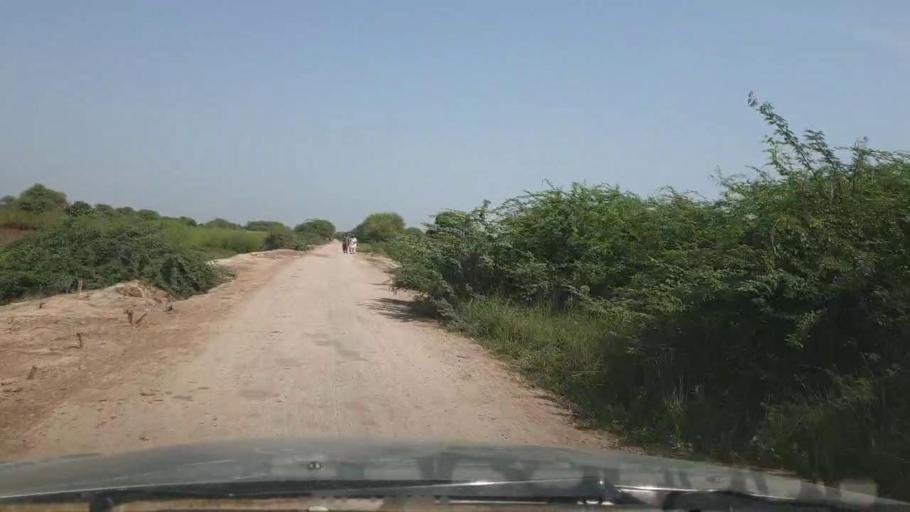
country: PK
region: Sindh
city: Tando Ghulam Ali
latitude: 25.1545
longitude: 68.9005
